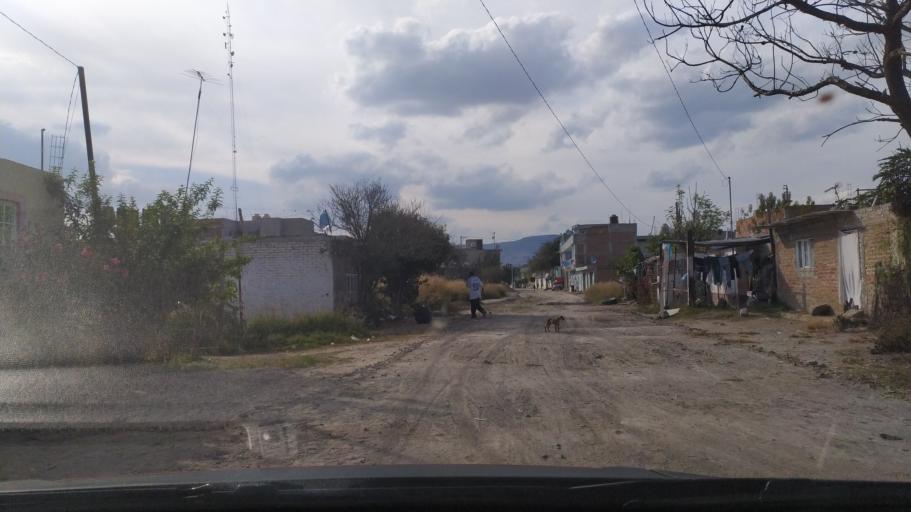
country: MX
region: Guanajuato
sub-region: San Francisco del Rincon
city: Fraccionamiento la Mezquitera
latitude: 21.0053
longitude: -101.8468
